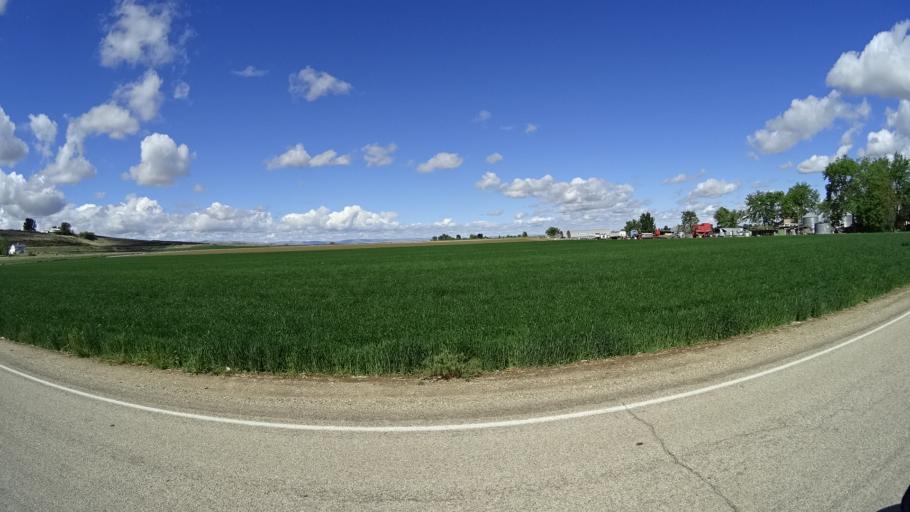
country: US
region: Idaho
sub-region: Ada County
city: Kuna
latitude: 43.4644
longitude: -116.4735
